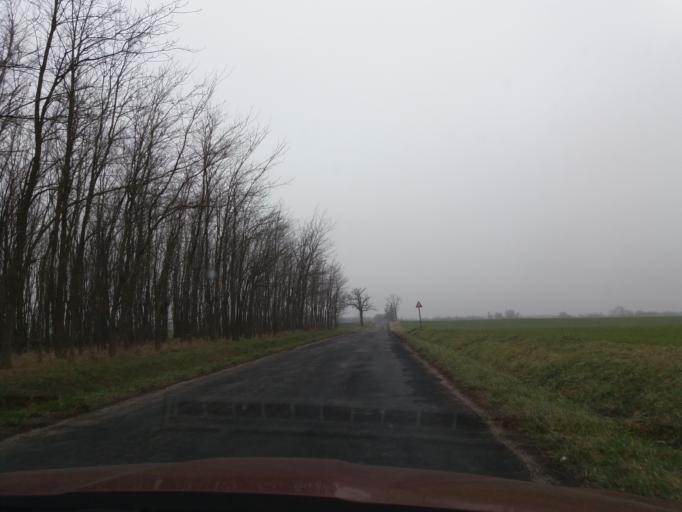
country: HU
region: Veszprem
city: Csabrendek
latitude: 47.0955
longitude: 17.2594
